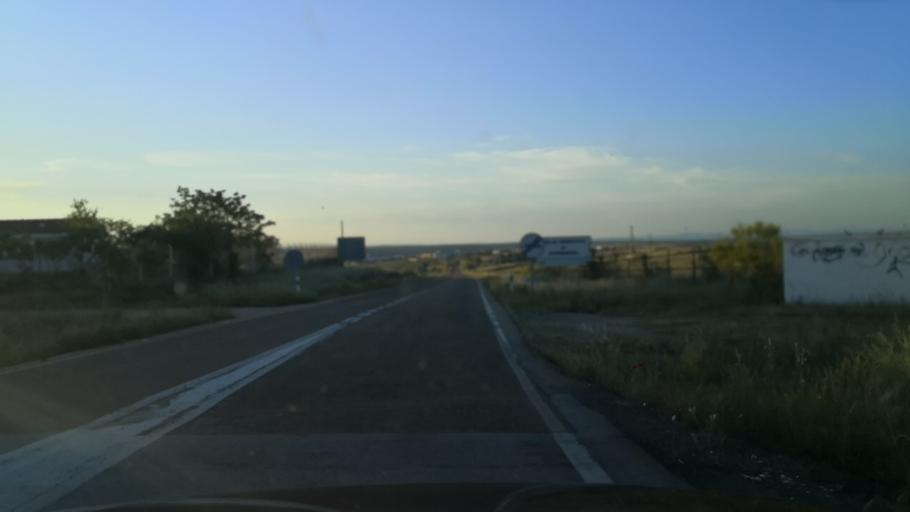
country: ES
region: Extremadura
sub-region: Provincia de Caceres
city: Salorino
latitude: 39.5155
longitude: -7.0479
